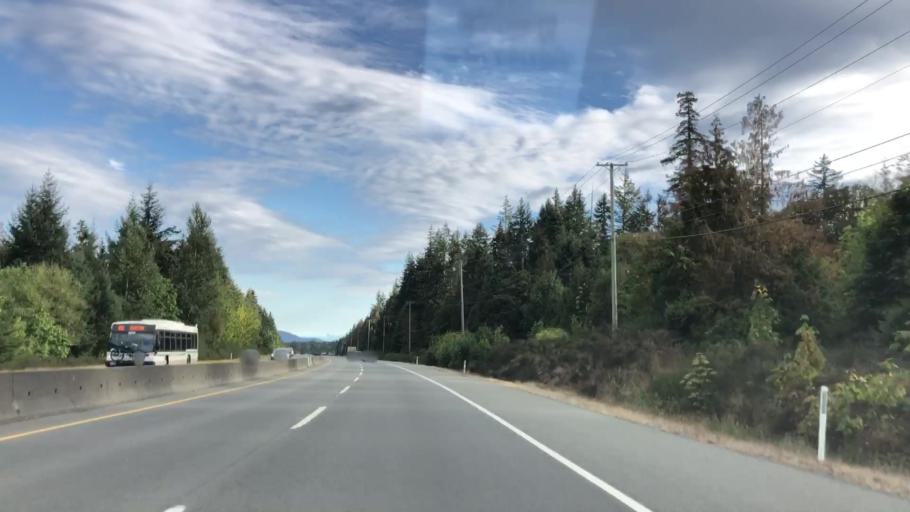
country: CA
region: British Columbia
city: North Saanich
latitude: 48.6221
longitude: -123.5462
